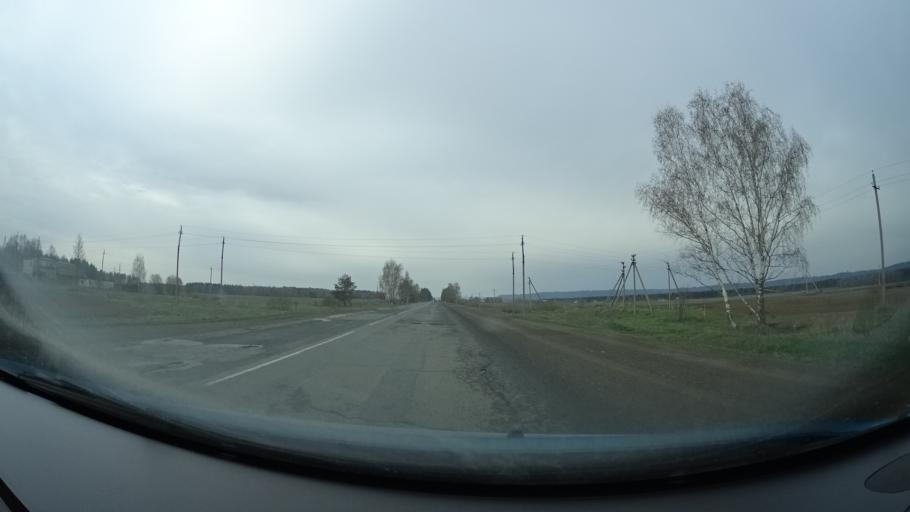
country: RU
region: Perm
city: Ust'-Kachka
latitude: 58.0582
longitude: 55.6080
